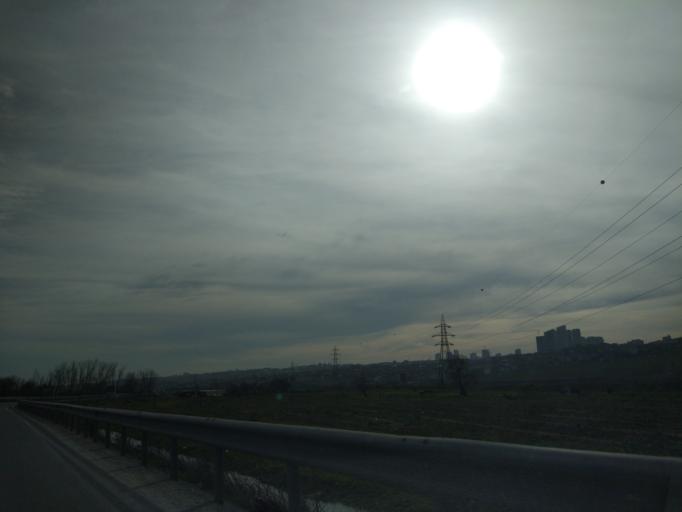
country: TR
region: Istanbul
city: Esenyurt
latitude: 41.0555
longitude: 28.7016
